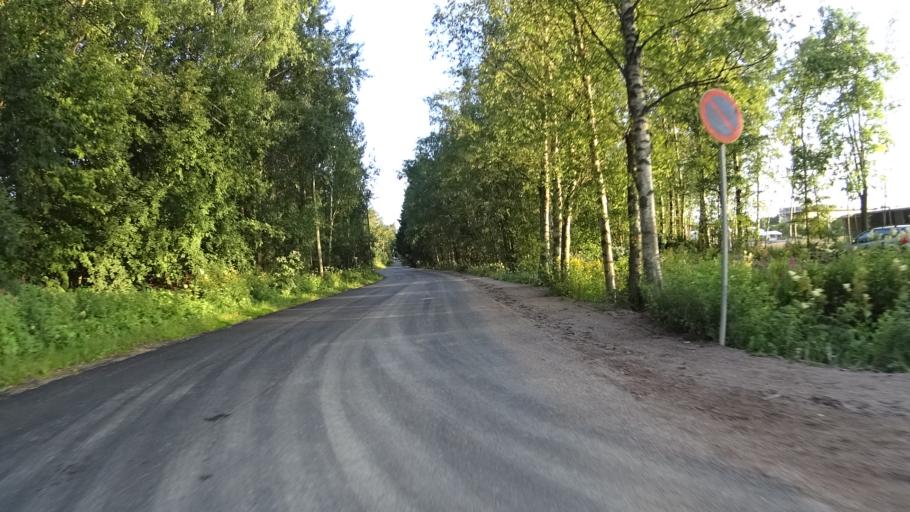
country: FI
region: Uusimaa
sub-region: Helsinki
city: Teekkarikylae
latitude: 60.2172
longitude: 24.8473
